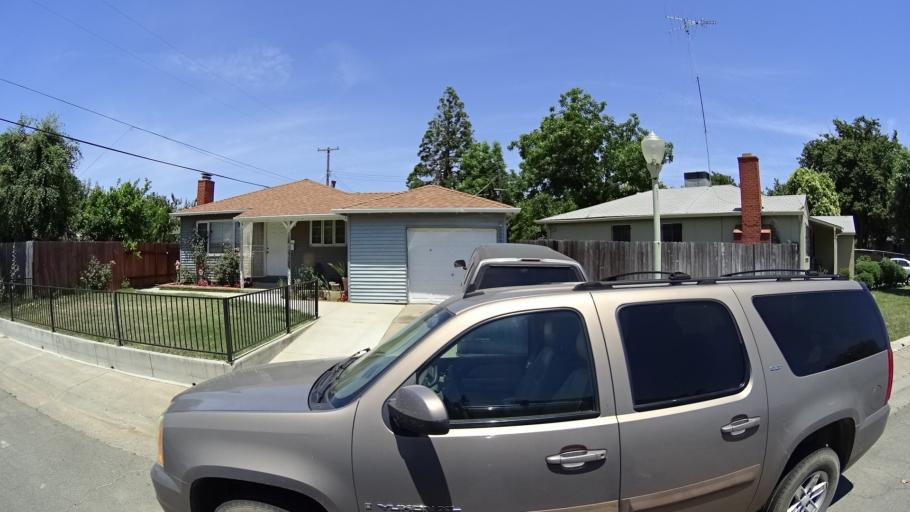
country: US
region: California
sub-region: Sacramento County
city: Florin
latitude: 38.5272
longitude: -121.4219
